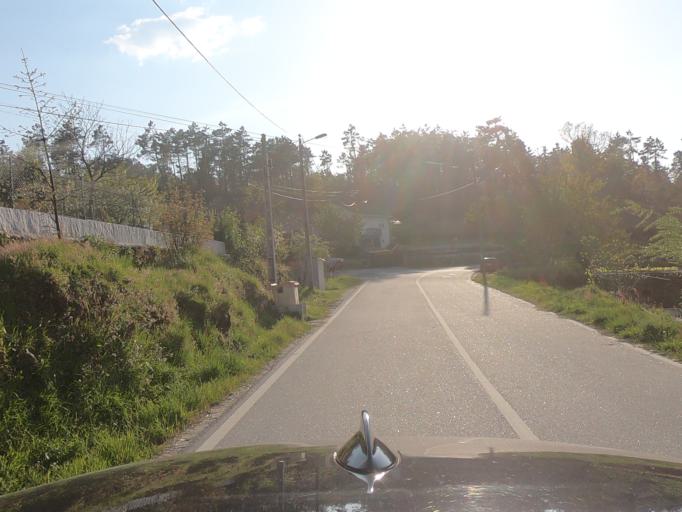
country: PT
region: Vila Real
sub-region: Santa Marta de Penaguiao
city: Santa Marta de Penaguiao
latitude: 41.2818
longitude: -7.8179
